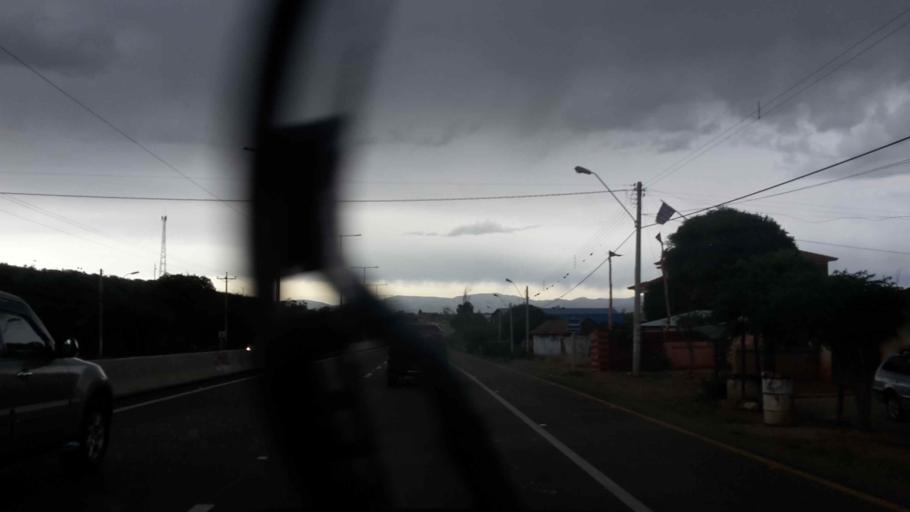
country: BO
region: Cochabamba
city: Tarata
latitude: -17.5384
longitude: -66.0705
